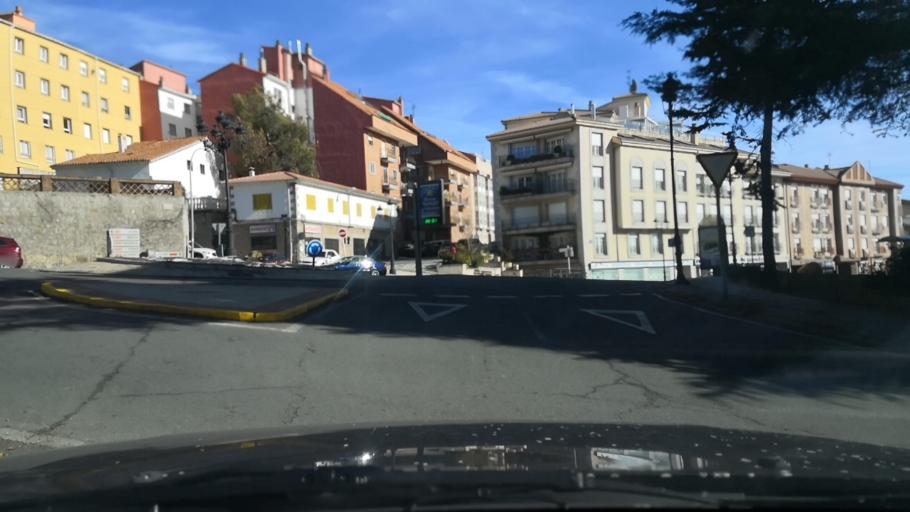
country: ES
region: Castille and Leon
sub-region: Provincia de Avila
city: Avila
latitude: 40.6539
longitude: -4.6852
